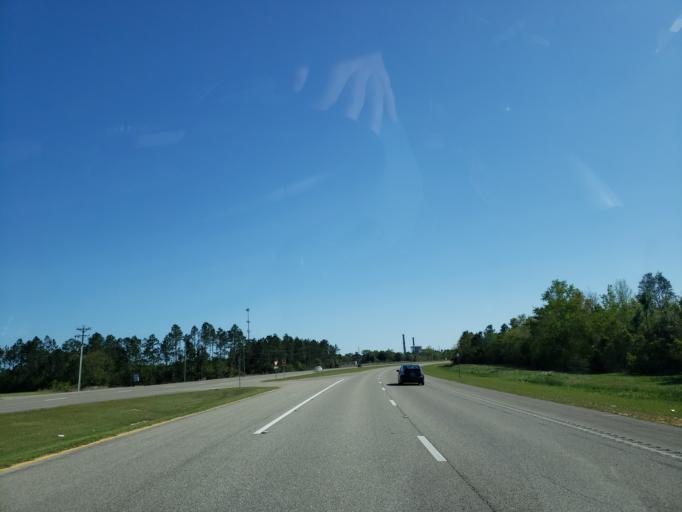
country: US
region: Mississippi
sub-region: Harrison County
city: West Gulfport
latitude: 30.4624
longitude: -89.0269
